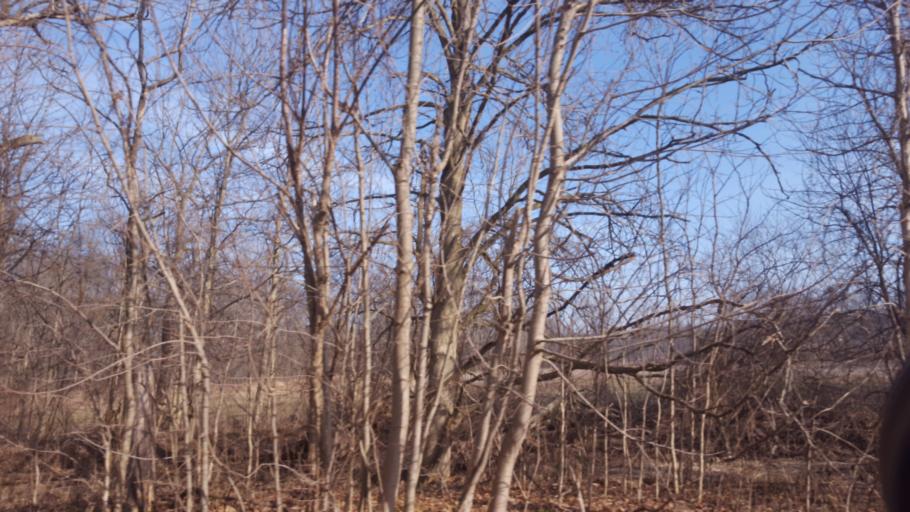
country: US
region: Ohio
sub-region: Crawford County
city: Crestline
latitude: 40.7043
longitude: -82.6892
